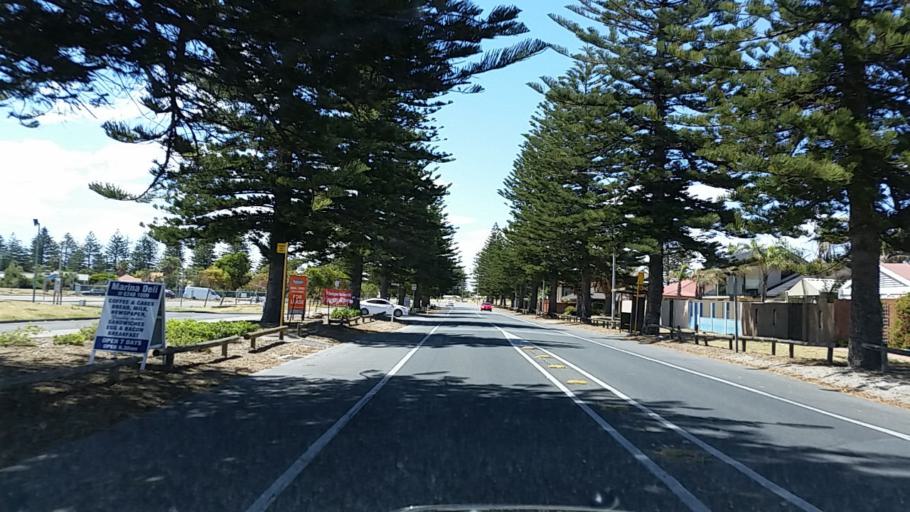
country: AU
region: South Australia
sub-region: Port Adelaide Enfield
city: Birkenhead
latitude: -34.7864
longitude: 138.4897
